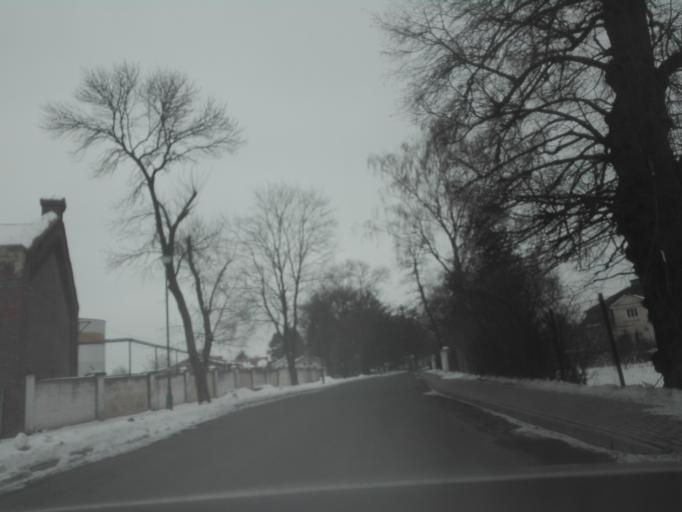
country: PL
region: Lublin Voivodeship
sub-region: Powiat hrubieszowski
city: Horodlo
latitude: 50.8430
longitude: 24.0352
